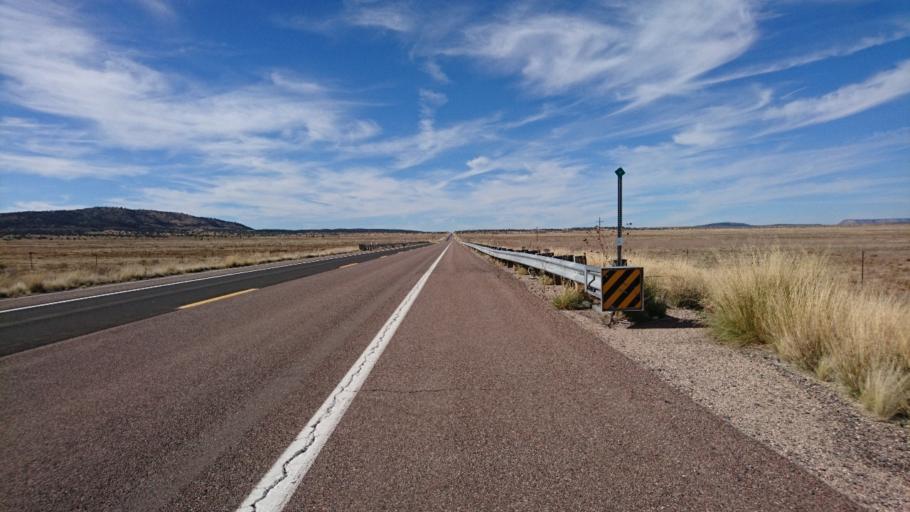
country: US
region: Arizona
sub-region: Mohave County
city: Peach Springs
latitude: 35.4822
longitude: -113.1438
